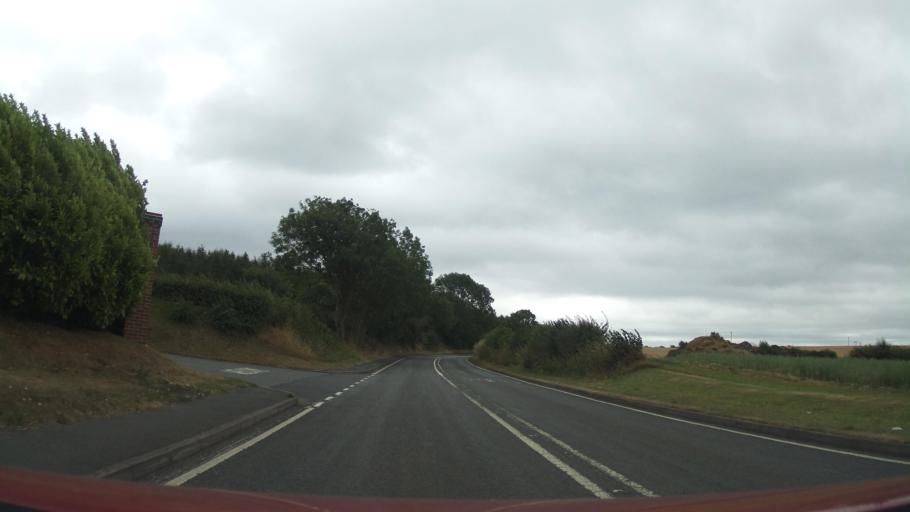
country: GB
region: England
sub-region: Leicestershire
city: Ashby de la Zouch
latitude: 52.7599
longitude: -1.4958
